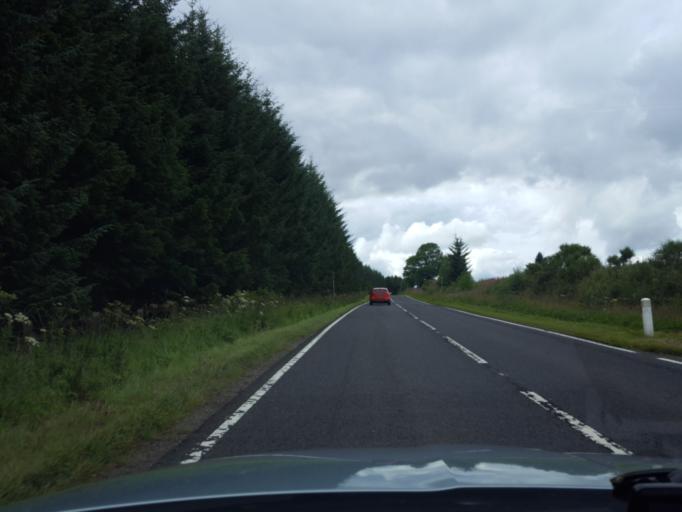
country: GB
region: Scotland
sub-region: Moray
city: Rothes
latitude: 57.4363
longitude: -3.3015
